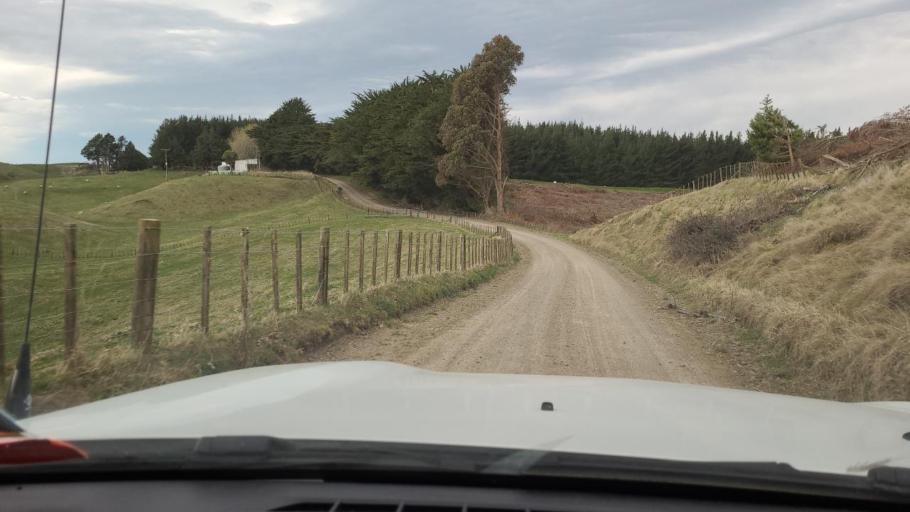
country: NZ
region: Hawke's Bay
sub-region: Napier City
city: Napier
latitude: -39.2271
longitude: 177.0008
